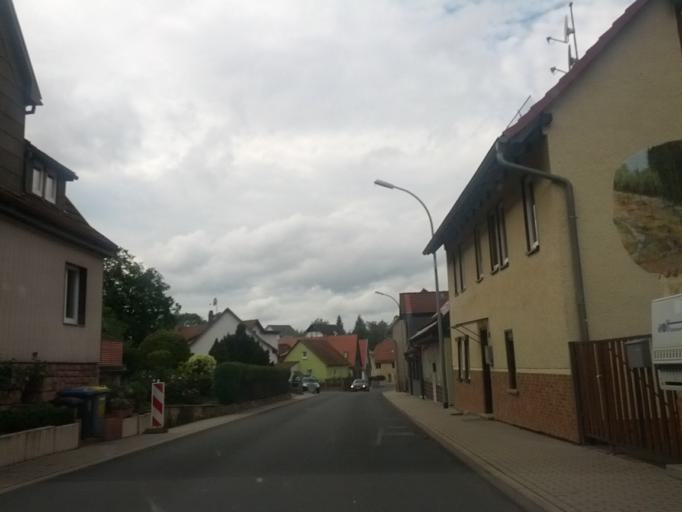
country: DE
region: Thuringia
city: Bad Salzungen
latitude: 50.8195
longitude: 10.2599
